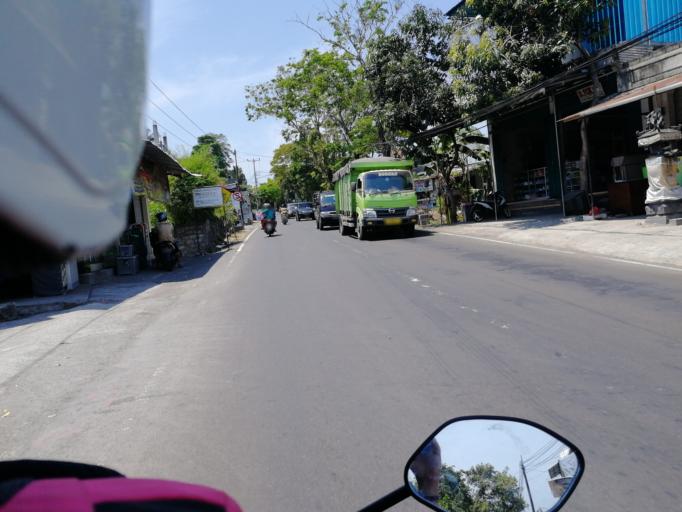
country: ID
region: Bali
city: Subagan
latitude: -8.4545
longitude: 115.5966
